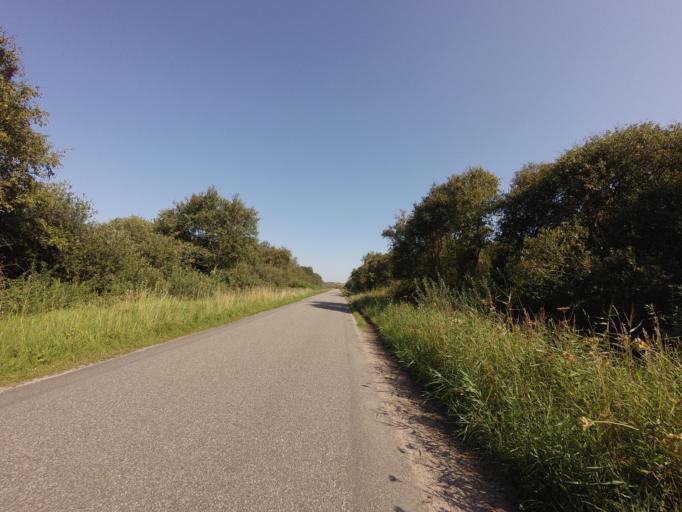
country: NL
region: Friesland
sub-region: Gemeente Schiermonnikoog
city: Schiermonnikoog
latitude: 53.4937
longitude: 6.1851
